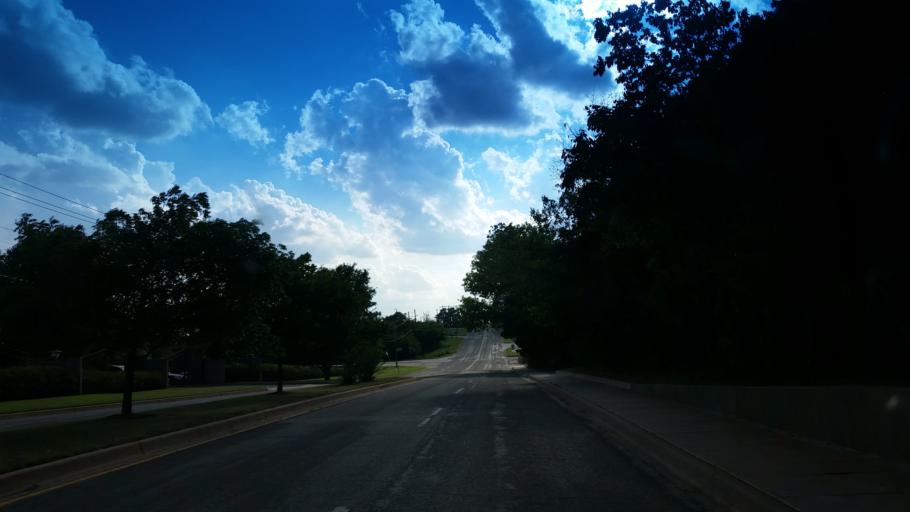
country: US
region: Oklahoma
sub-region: Oklahoma County
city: Nichols Hills
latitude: 35.5368
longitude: -97.4835
